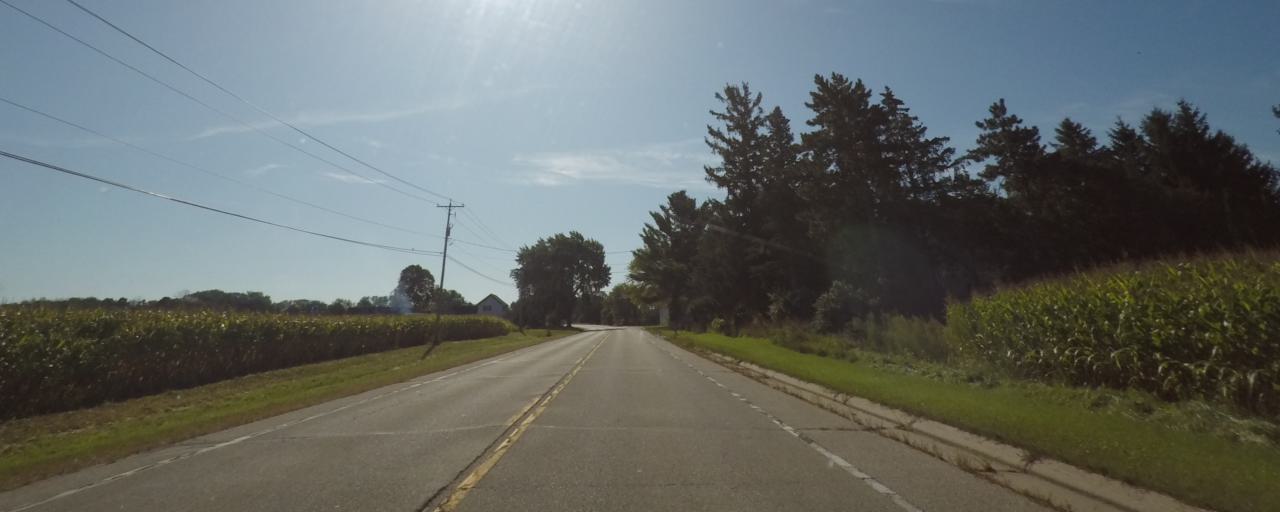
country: US
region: Wisconsin
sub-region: Waukesha County
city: Dousman
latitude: 43.0243
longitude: -88.5025
